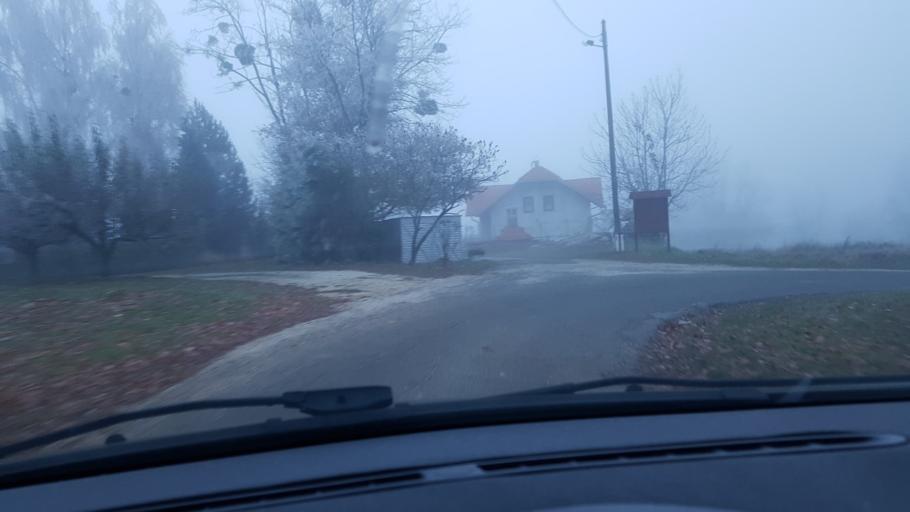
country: HR
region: Krapinsko-Zagorska
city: Pregrada
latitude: 46.1932
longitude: 15.7477
